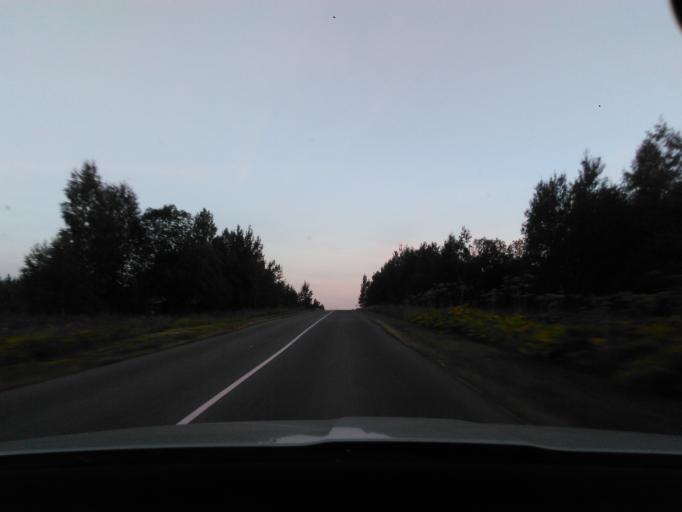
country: RU
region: Moskovskaya
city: Klin
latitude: 56.2370
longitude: 36.7520
